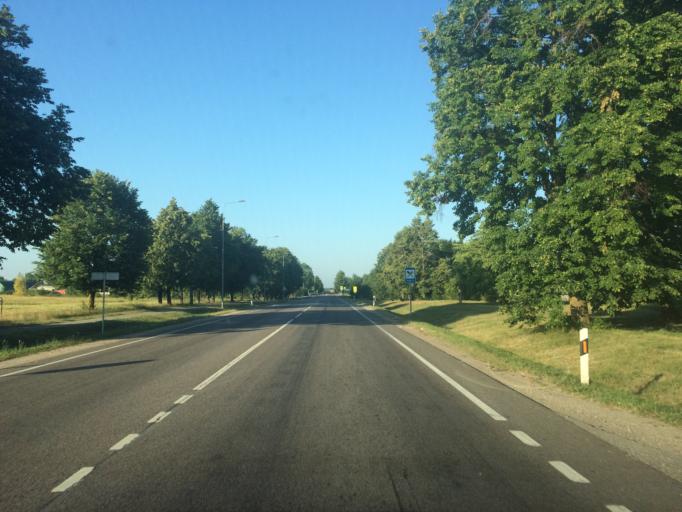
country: LT
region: Vilnius County
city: Ukmerge
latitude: 55.3122
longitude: 24.8688
